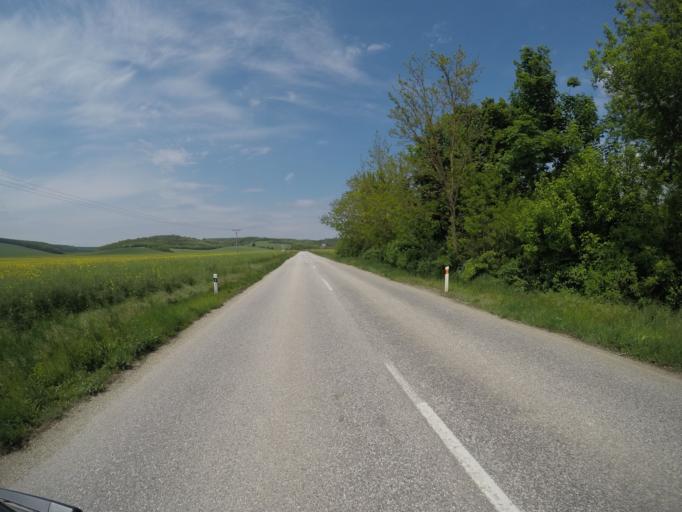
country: HU
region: Komarom-Esztergom
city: Esztergom
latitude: 47.9326
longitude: 18.7463
